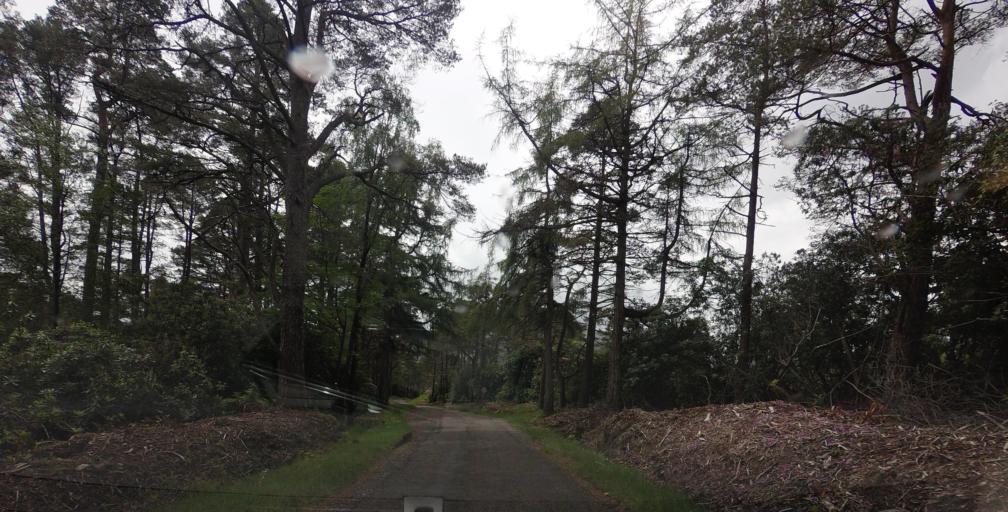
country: GB
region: Scotland
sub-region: Highland
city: Fort William
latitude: 56.7727
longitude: -5.2198
